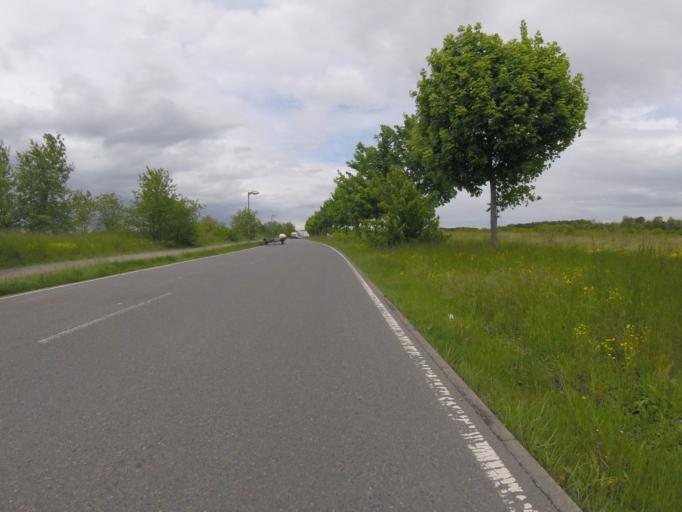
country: DE
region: Brandenburg
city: Konigs Wusterhausen
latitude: 52.3034
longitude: 13.5989
